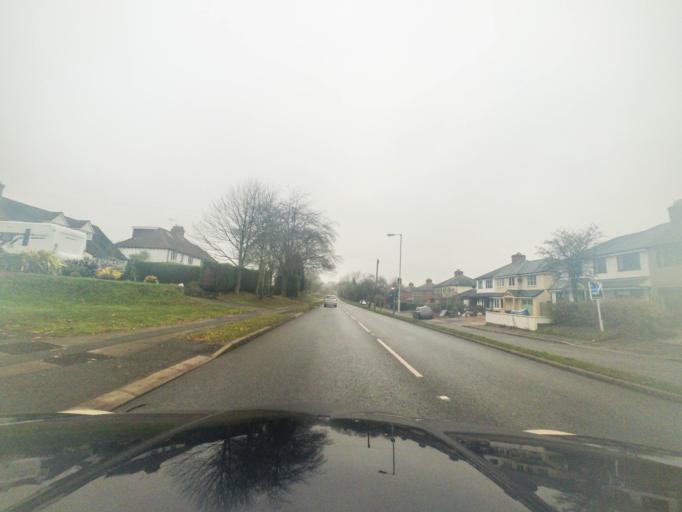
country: GB
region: England
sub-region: Solihull
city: Balsall Common
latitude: 52.3885
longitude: -1.6664
